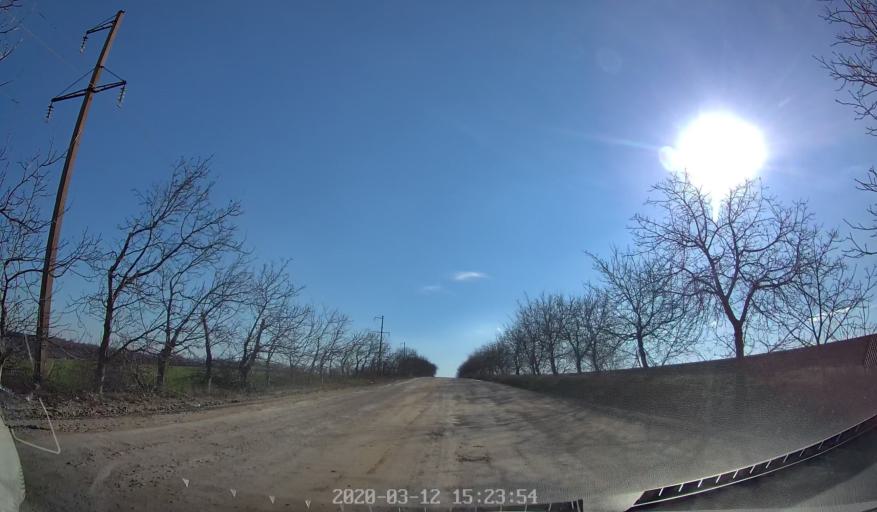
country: MD
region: Chisinau
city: Ciorescu
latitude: 47.1894
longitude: 28.9151
